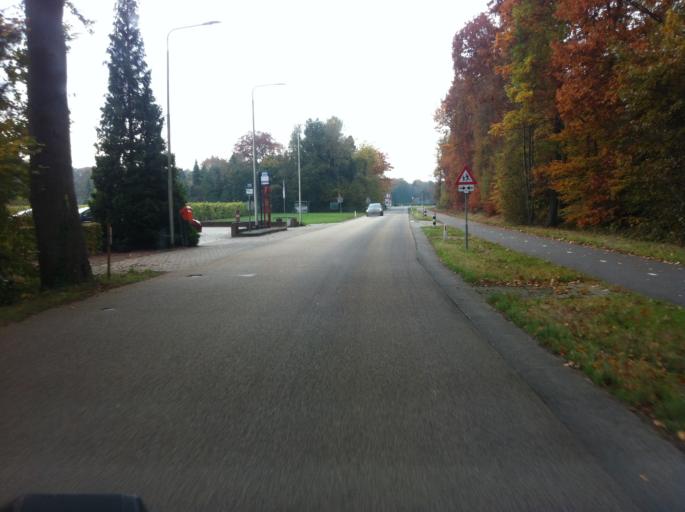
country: NL
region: Gelderland
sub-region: Gemeente Winterswijk
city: Winterswijk
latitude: 51.9913
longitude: 6.7711
